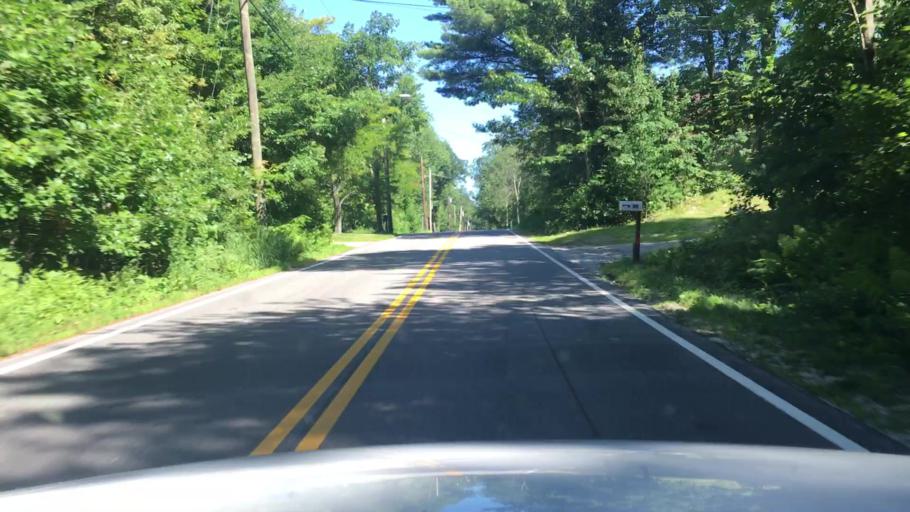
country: US
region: New Hampshire
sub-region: Merrimack County
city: South Hooksett
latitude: 43.0378
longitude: -71.4029
